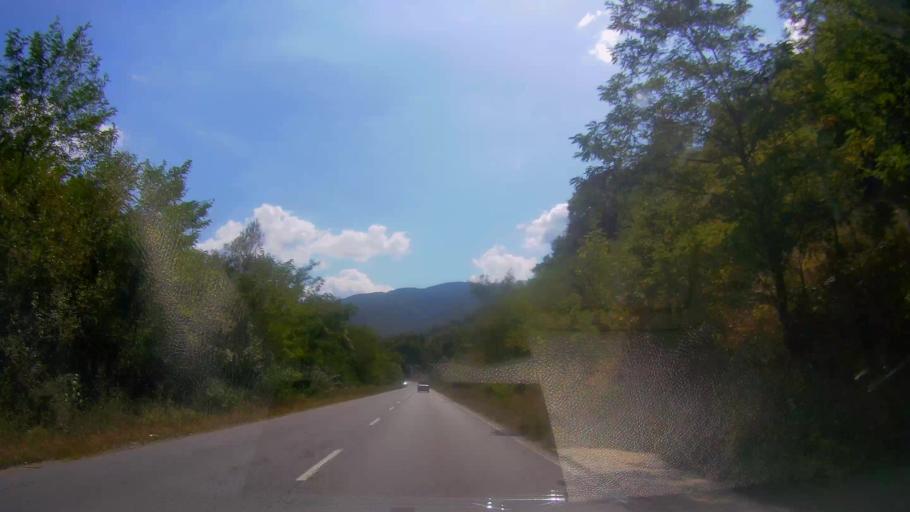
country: BG
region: Stara Zagora
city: Gurkovo
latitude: 42.7210
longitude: 25.7144
